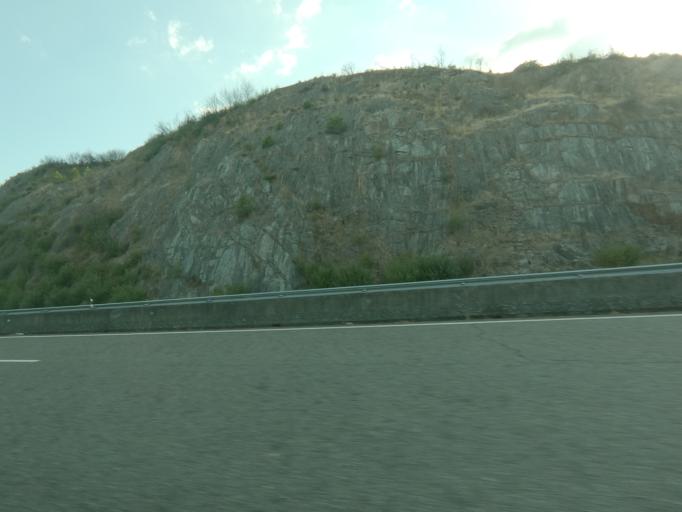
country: ES
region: Galicia
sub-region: Provincia de Ourense
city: Oimbra
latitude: 41.9381
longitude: -7.4991
